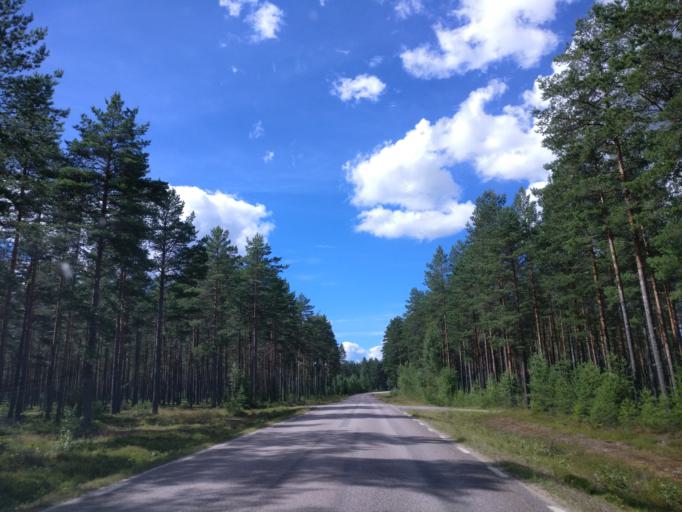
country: SE
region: Vaermland
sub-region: Hagfors Kommun
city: Ekshaerad
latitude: 60.0417
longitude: 13.5173
